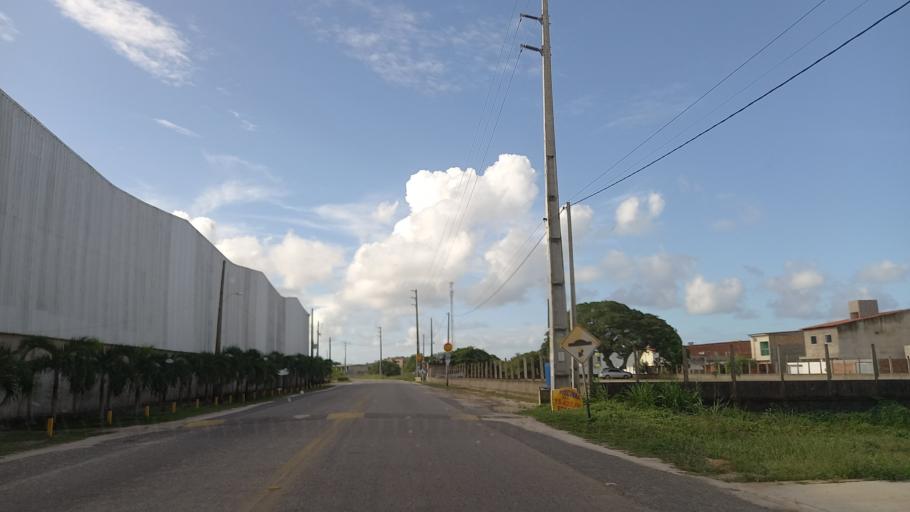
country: BR
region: Pernambuco
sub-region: Tamandare
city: Tamandare
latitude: -8.7273
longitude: -35.0954
